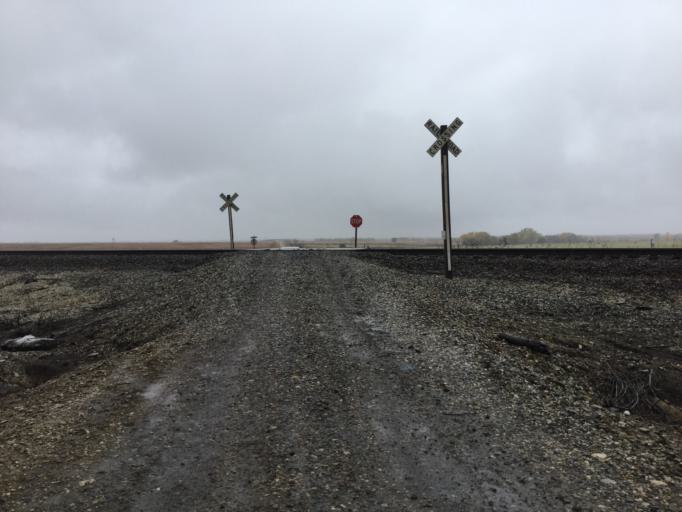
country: US
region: Kansas
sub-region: Butler County
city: El Dorado
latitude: 38.0137
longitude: -96.6604
